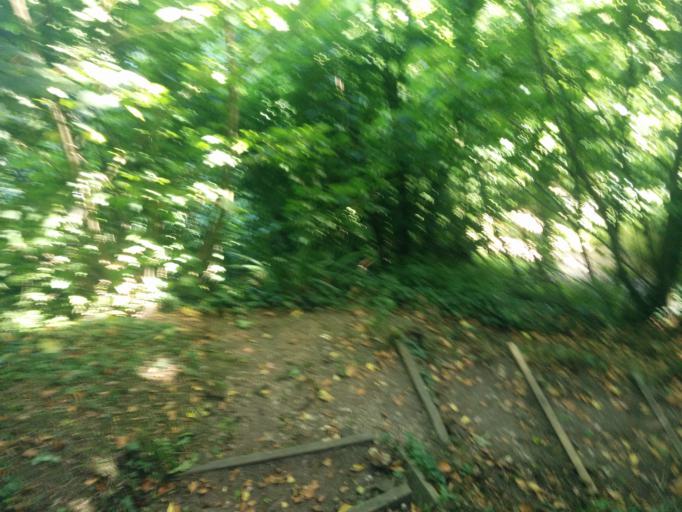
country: GB
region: England
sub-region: Dorset
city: Lyme Regis
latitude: 50.7199
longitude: -2.9553
